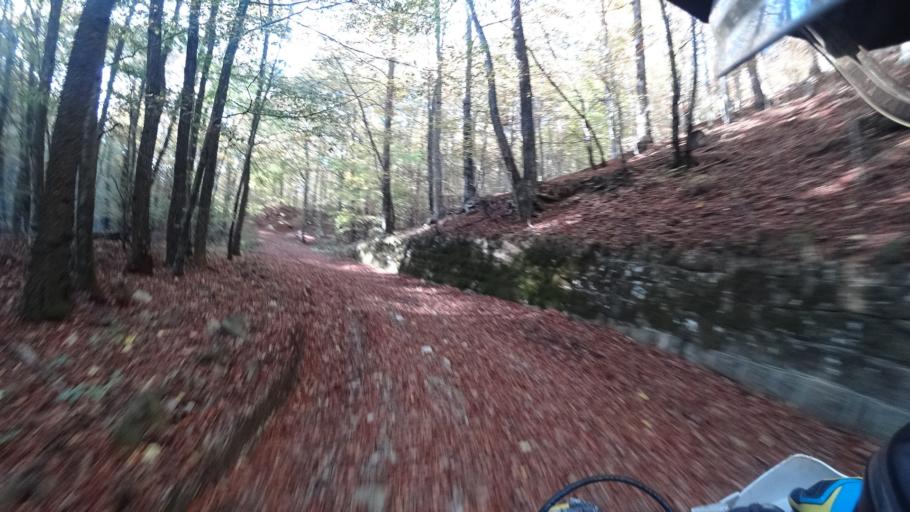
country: HR
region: Primorsko-Goranska
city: Klana
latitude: 45.4942
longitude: 14.3949
